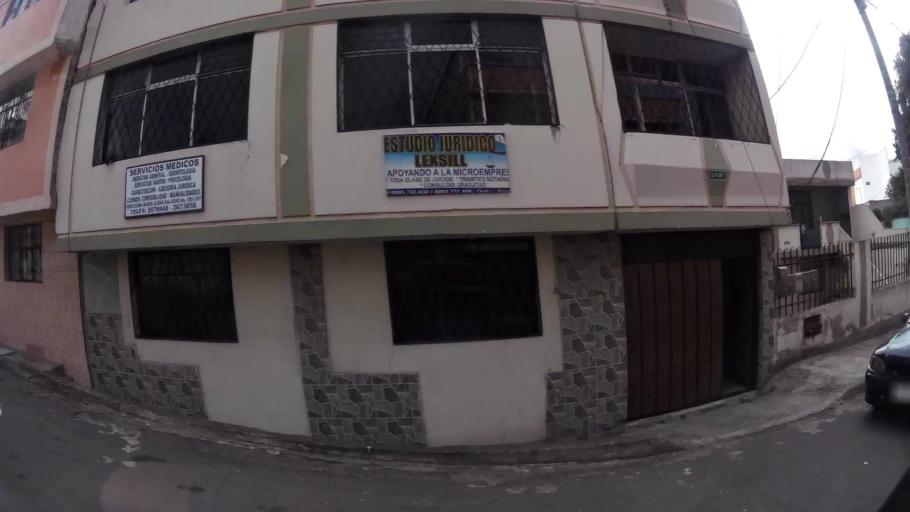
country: EC
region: Pichincha
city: Quito
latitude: -0.2863
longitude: -78.5402
